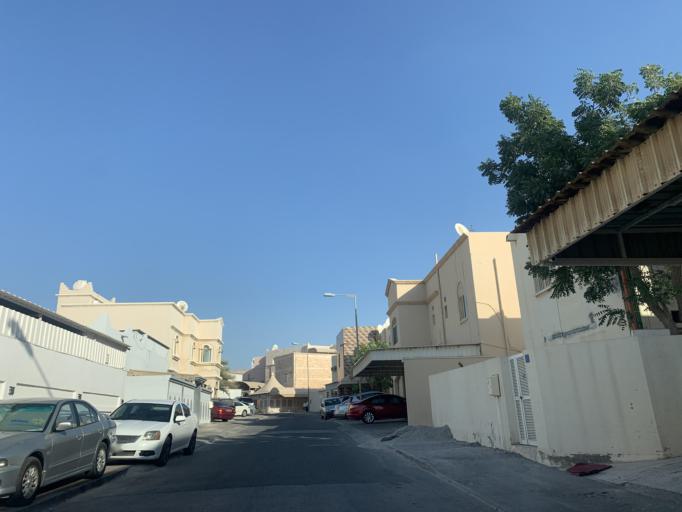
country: BH
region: Central Governorate
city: Madinat Hamad
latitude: 26.1092
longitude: 50.5067
